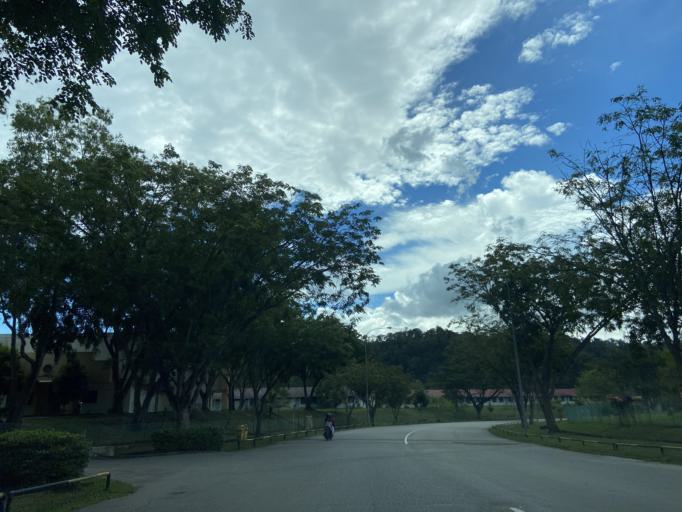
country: SG
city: Singapore
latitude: 1.0568
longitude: 104.0273
